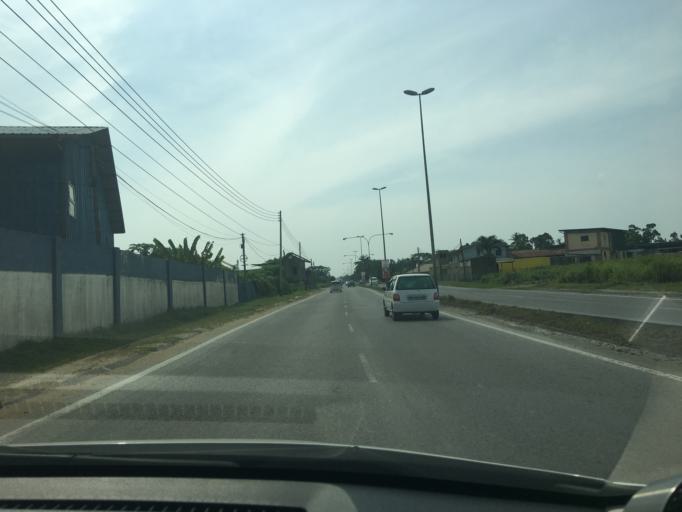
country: MY
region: Sarawak
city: Kuching
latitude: 1.5094
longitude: 110.2776
